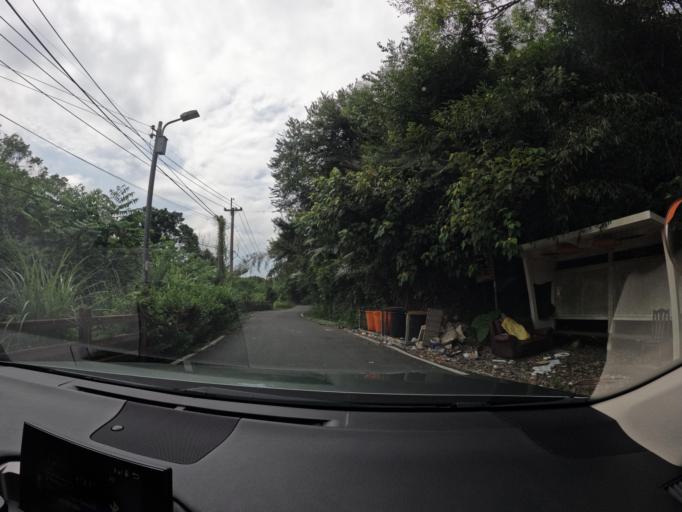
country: TW
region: Taiwan
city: Fengyuan
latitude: 24.3449
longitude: 120.8766
